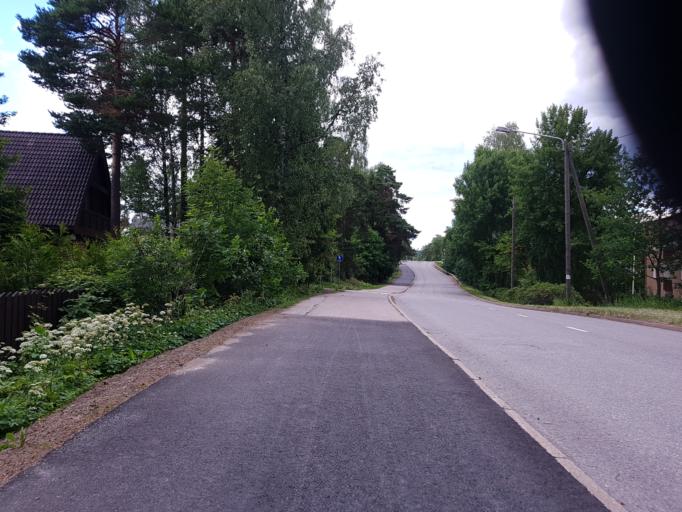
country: FI
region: Uusimaa
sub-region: Helsinki
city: Teekkarikylae
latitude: 60.2784
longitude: 24.8750
